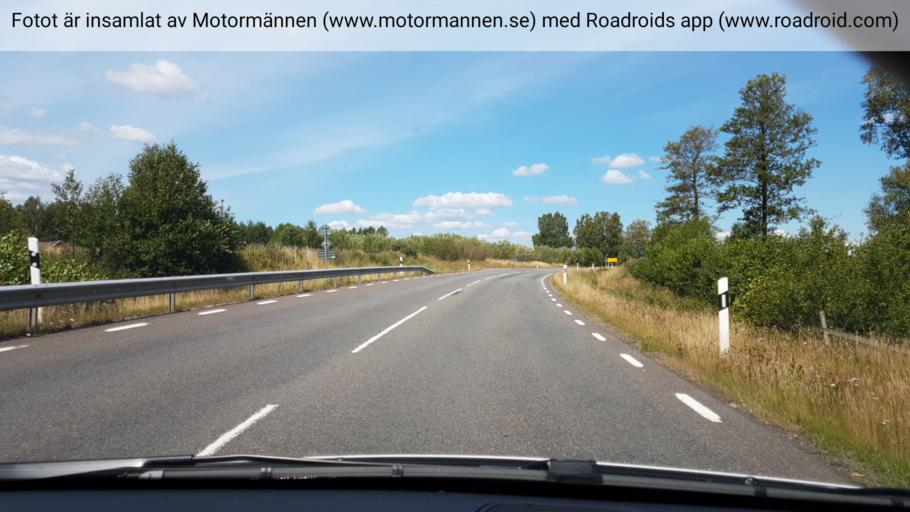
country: SE
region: Vaestra Goetaland
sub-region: Tibro Kommun
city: Tibro
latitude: 58.4830
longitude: 14.1687
